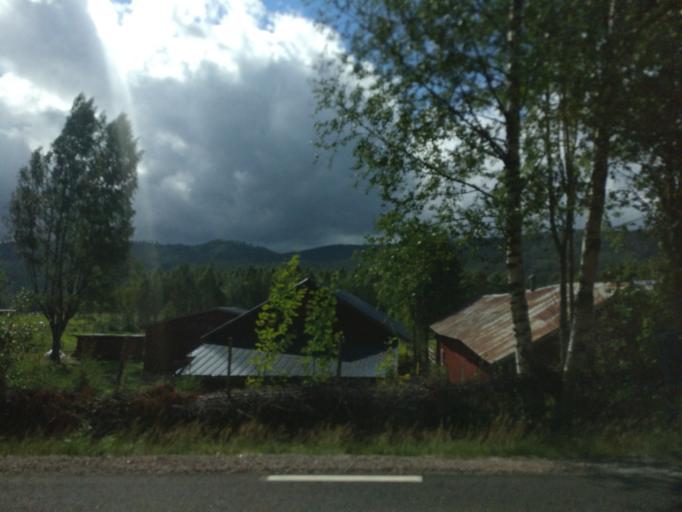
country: SE
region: Vaermland
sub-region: Hagfors Kommun
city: Ekshaerad
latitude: 60.3517
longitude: 13.3358
